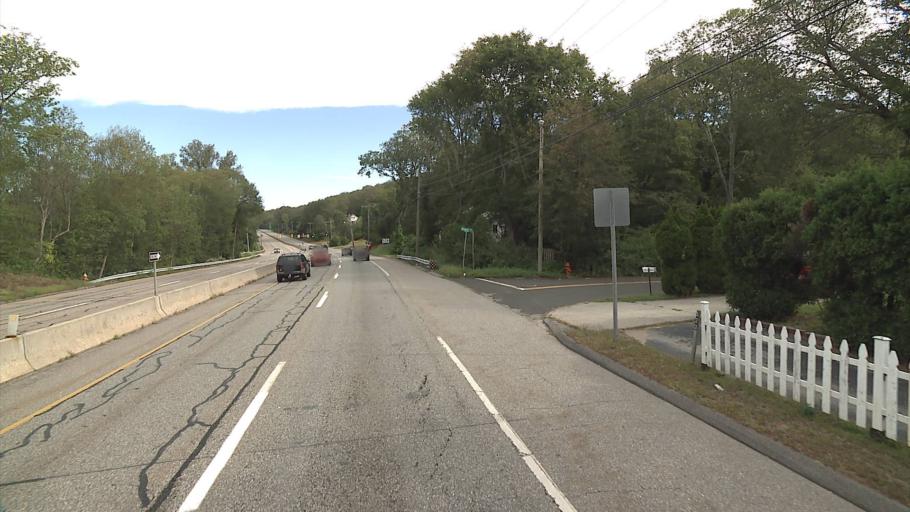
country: US
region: Connecticut
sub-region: New London County
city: Uncasville
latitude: 41.4021
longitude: -72.1058
